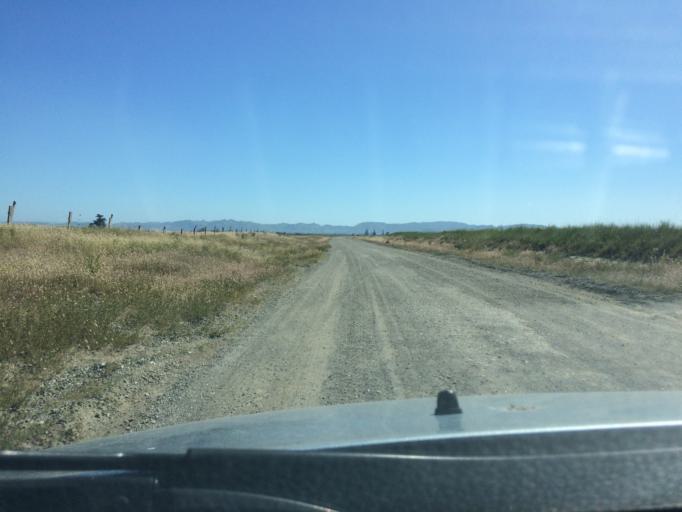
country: NZ
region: Gisborne
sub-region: Gisborne District
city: Gisborne
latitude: -38.7077
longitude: 177.9438
